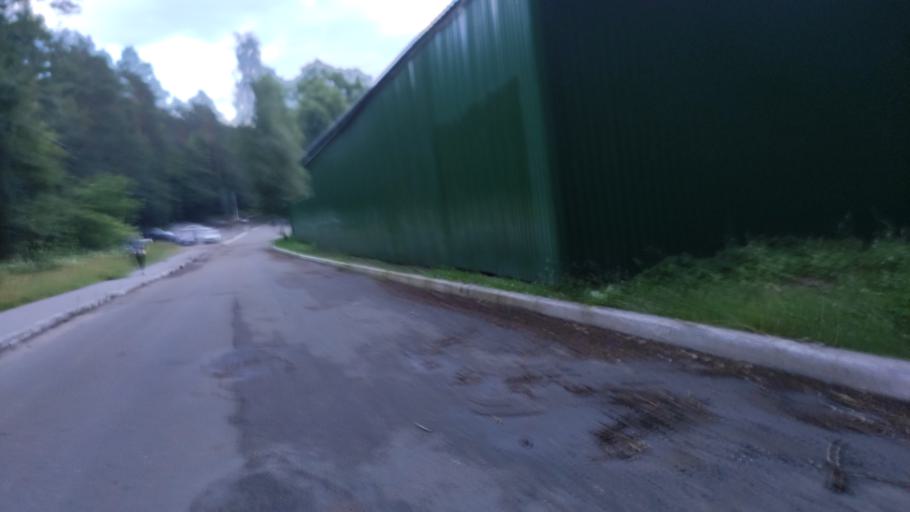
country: BY
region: Minsk
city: Zhdanovichy
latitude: 53.9683
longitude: 27.4304
